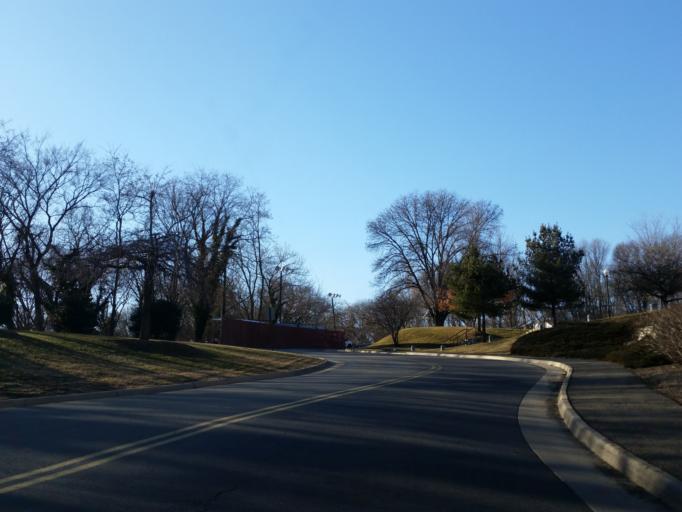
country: US
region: Virginia
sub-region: Arlington County
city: Arlington
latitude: 38.9061
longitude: -77.0764
